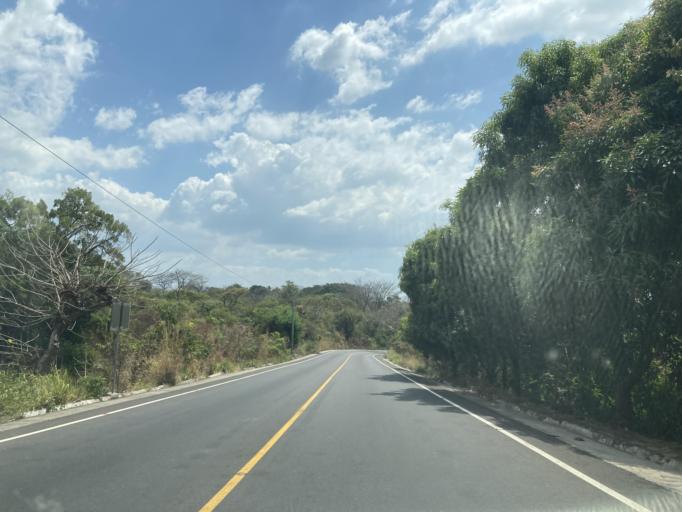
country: GT
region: Santa Rosa
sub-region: Municipio de Taxisco
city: Taxisco
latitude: 14.0703
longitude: -90.4731
